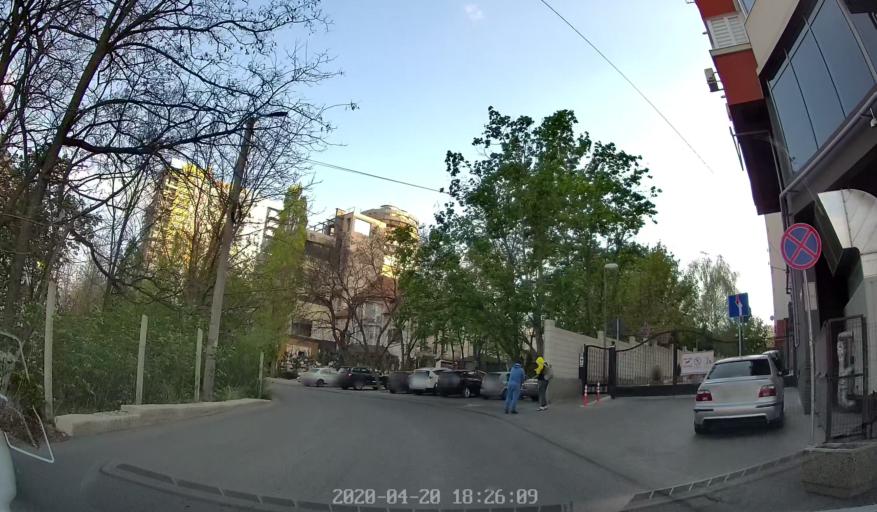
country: MD
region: Chisinau
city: Chisinau
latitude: 46.9927
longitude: 28.8369
